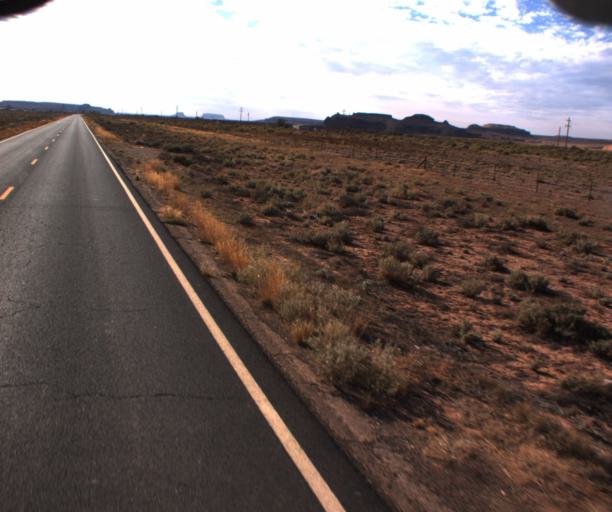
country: US
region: Arizona
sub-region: Apache County
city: Many Farms
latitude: 36.7457
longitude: -109.6402
